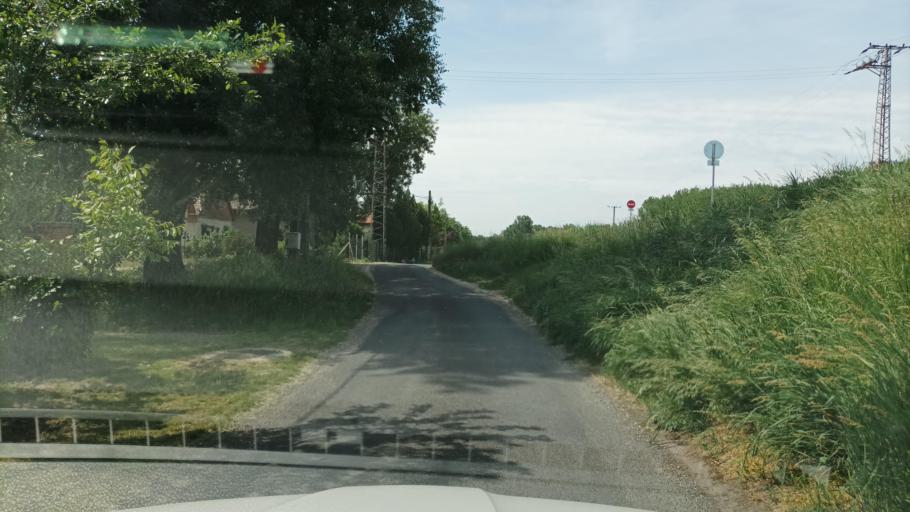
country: HU
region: Pest
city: Domsod
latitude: 47.0955
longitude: 18.9937
